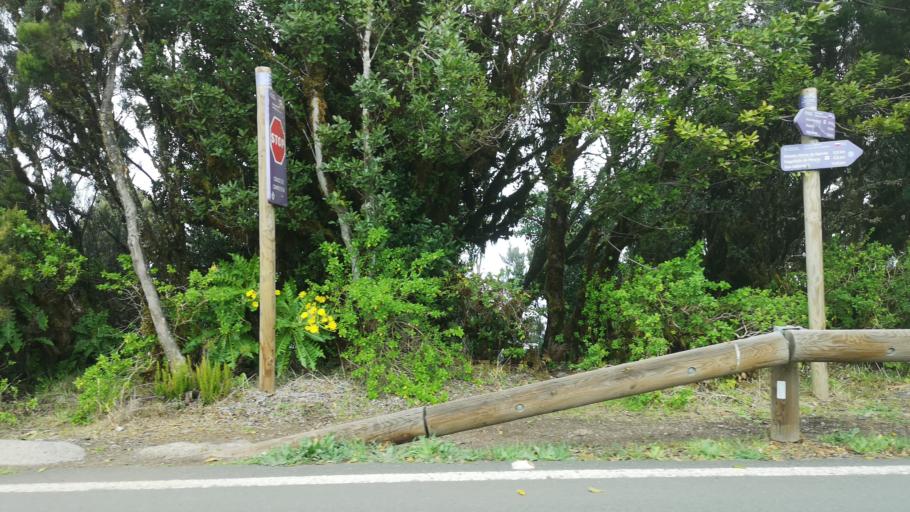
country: ES
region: Canary Islands
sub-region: Provincia de Santa Cruz de Tenerife
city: Alajero
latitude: 28.1092
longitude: -17.2238
